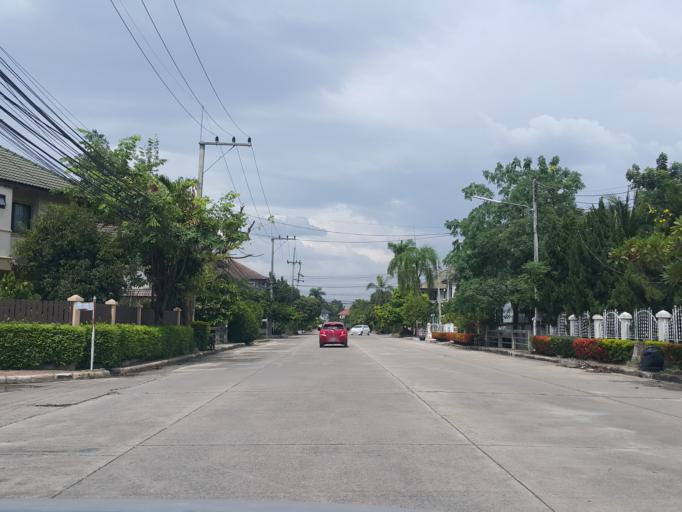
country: TH
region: Chiang Mai
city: Hang Dong
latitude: 18.7375
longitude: 98.9458
